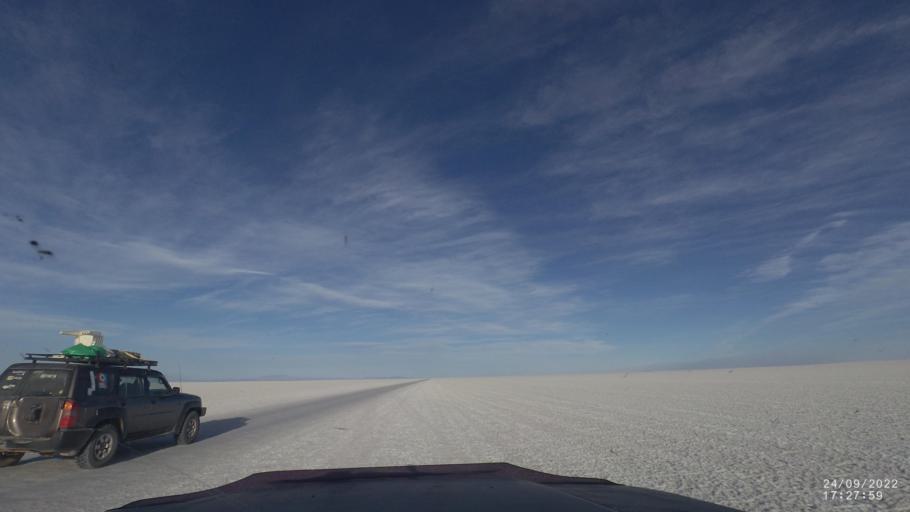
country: BO
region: Potosi
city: Colchani
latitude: -20.3016
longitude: -67.4368
